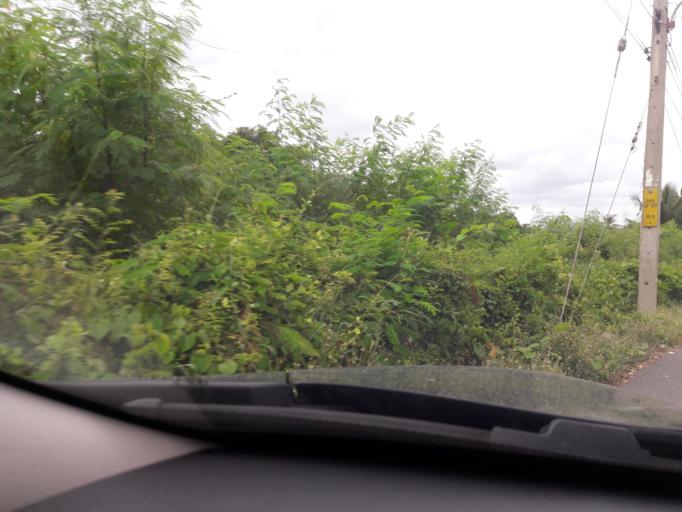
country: TH
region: Ratchaburi
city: Bang Phae
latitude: 13.6286
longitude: 99.9489
